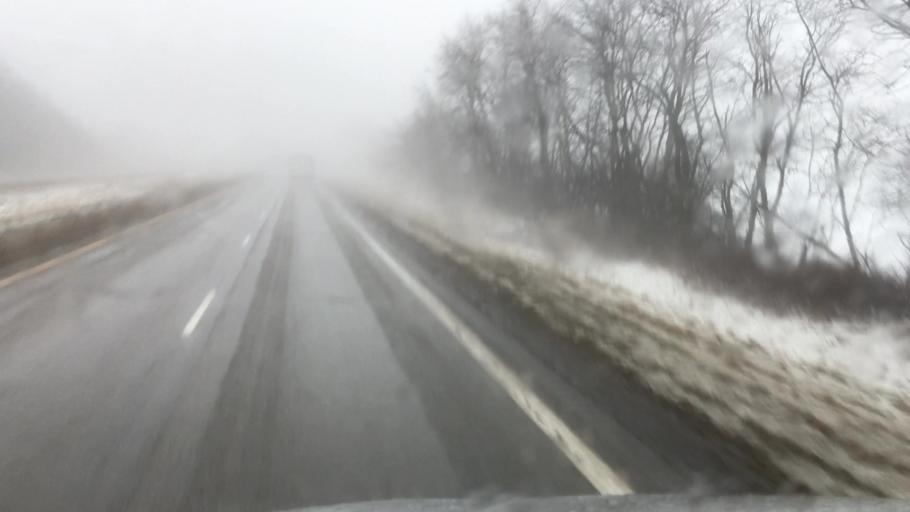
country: US
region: Indiana
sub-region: Newton County
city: Roselawn
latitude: 41.1288
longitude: -87.4531
